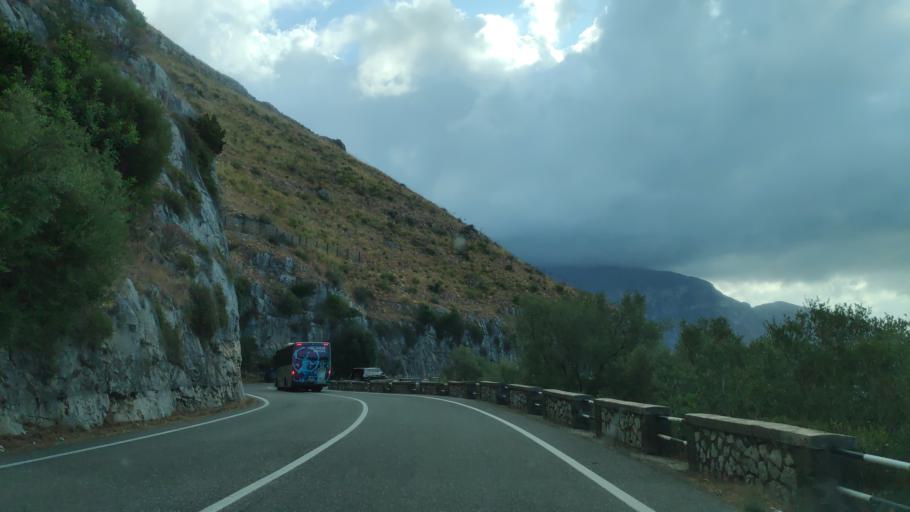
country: IT
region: Campania
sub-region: Provincia di Salerno
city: Positano
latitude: 40.6192
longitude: 14.4636
